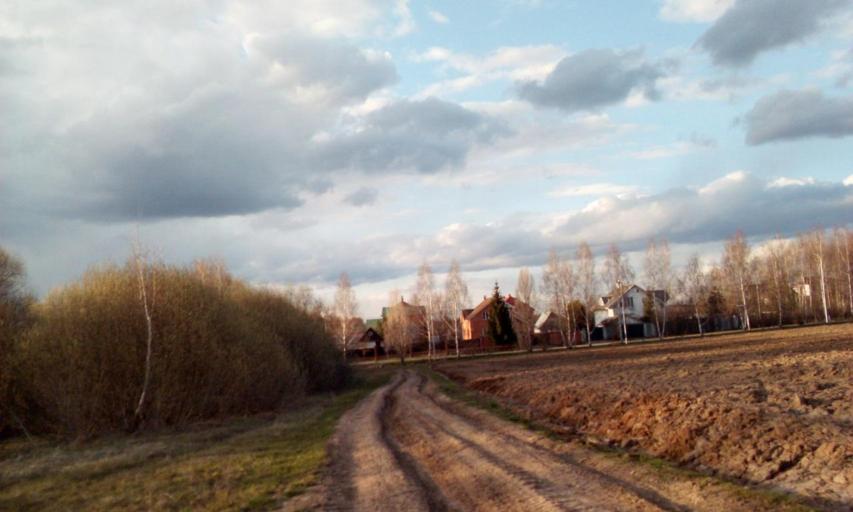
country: RU
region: Moskovskaya
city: Annino
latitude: 55.5500
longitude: 37.2360
